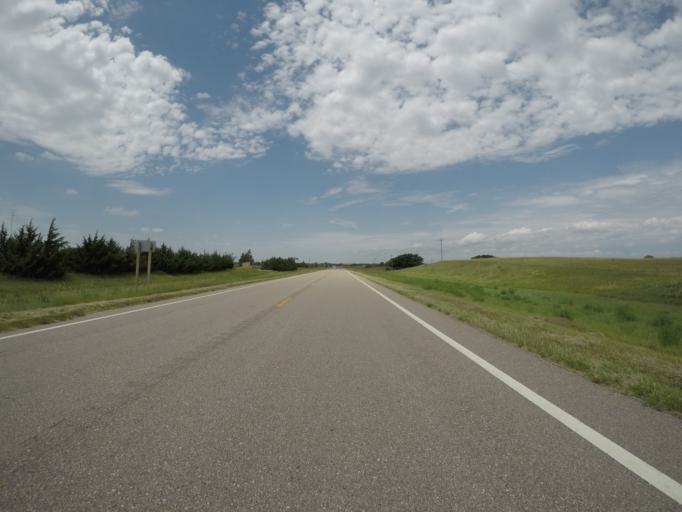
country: US
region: Kansas
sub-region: Graham County
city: Hill City
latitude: 39.3944
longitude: -99.6173
